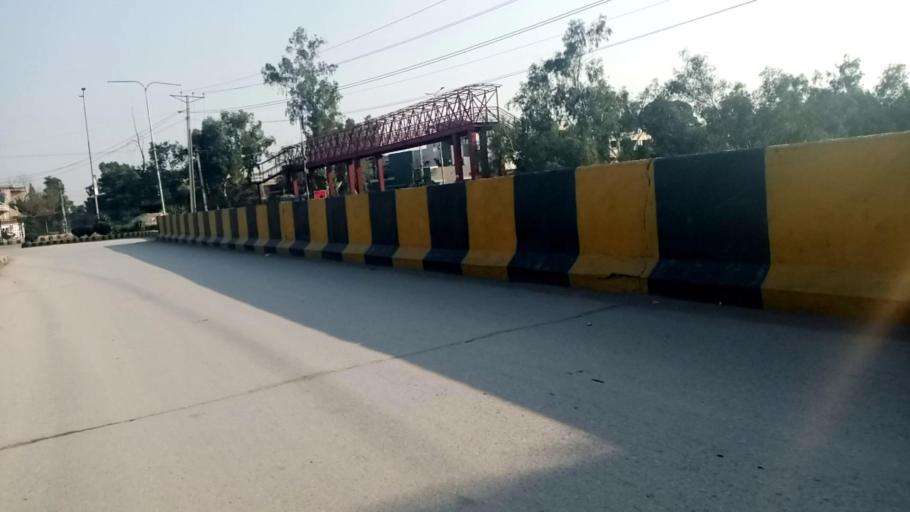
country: PK
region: Khyber Pakhtunkhwa
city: Peshawar
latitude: 33.9883
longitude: 71.4520
